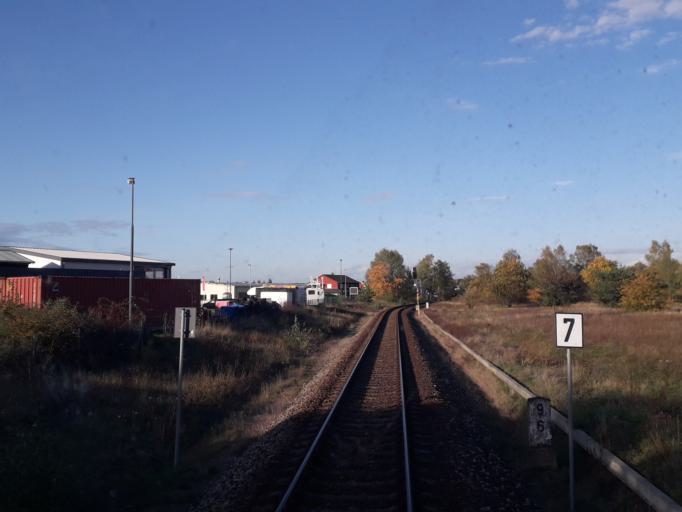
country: DE
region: Brandenburg
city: Perleberg
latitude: 53.0652
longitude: 11.8424
